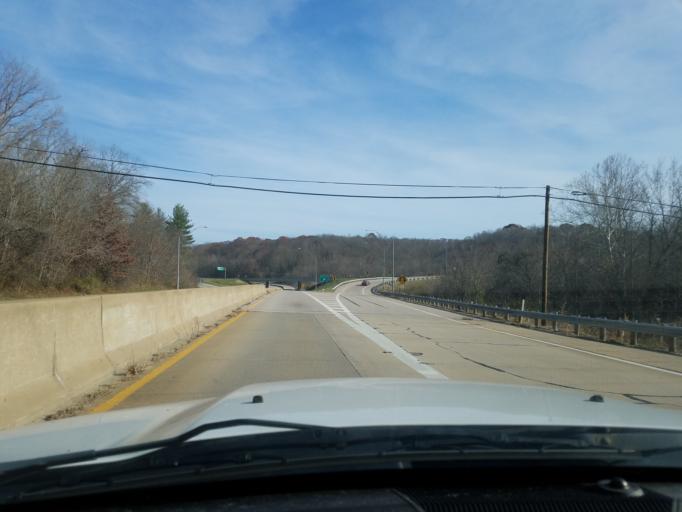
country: US
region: West Virginia
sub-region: Wood County
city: Washington
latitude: 39.2122
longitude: -81.8181
